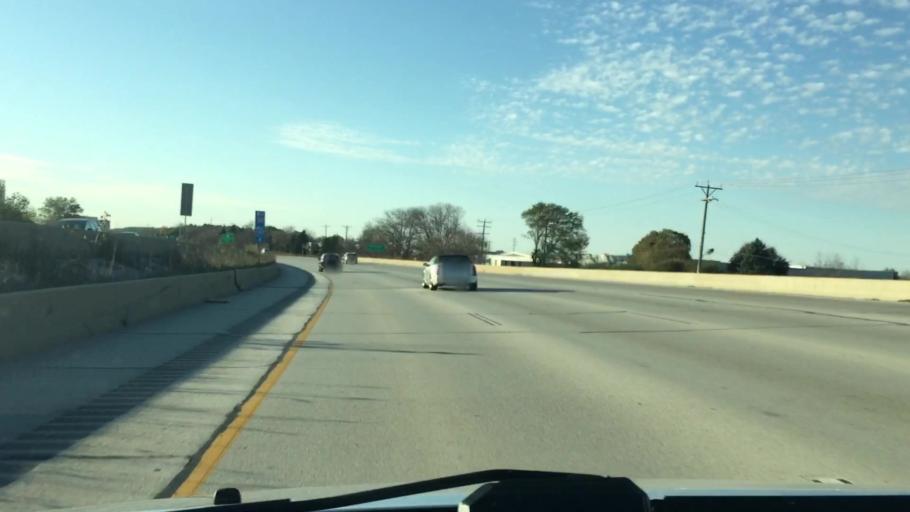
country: US
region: Wisconsin
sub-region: Waukesha County
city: Waukesha
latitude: 43.0398
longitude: -88.1786
